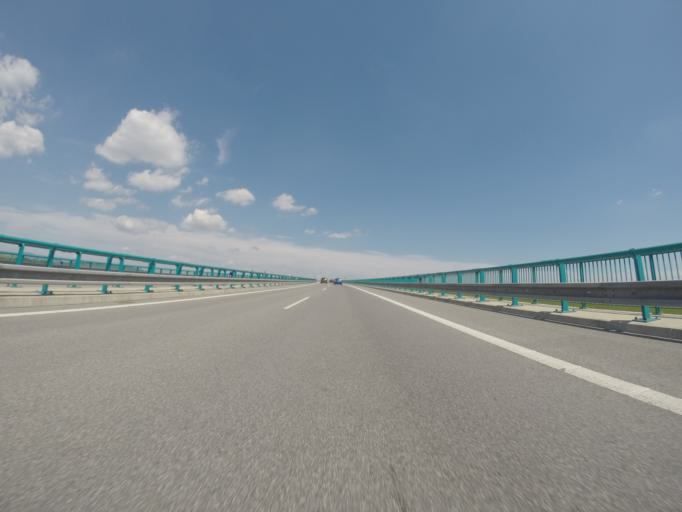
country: SK
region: Nitriansky
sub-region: Okres Nitra
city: Nitra
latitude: 48.3143
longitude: 18.1568
